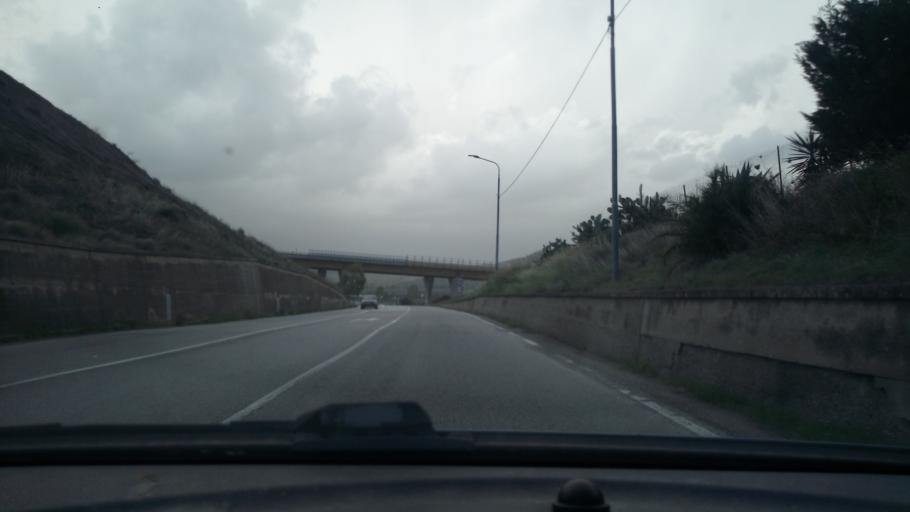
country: IT
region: Calabria
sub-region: Provincia di Catanzaro
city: Barone
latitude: 38.8588
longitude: 16.6302
